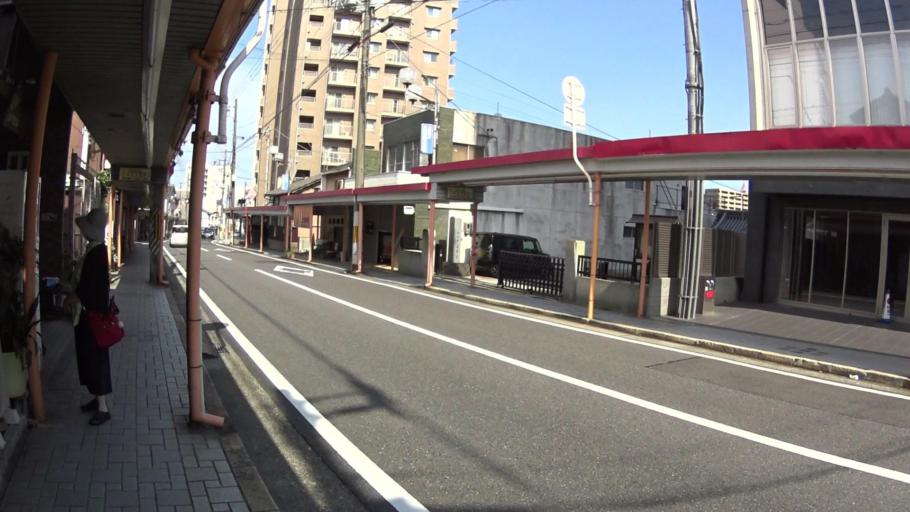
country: JP
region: Shiga Prefecture
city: Otsu-shi
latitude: 35.0116
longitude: 135.8529
